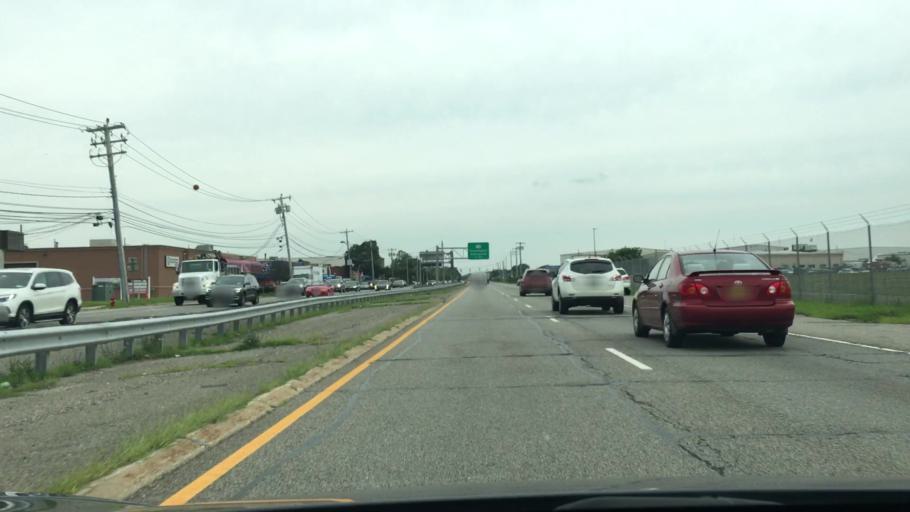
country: US
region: New York
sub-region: Suffolk County
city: East Farmingdale
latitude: 40.7195
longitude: -73.4137
